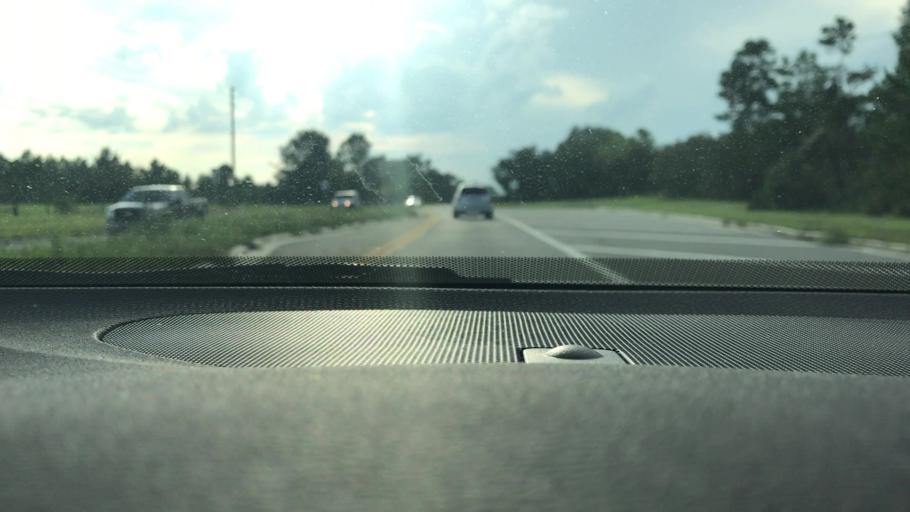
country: US
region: Florida
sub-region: Volusia County
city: Lake Helen
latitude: 28.9849
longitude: -81.2534
